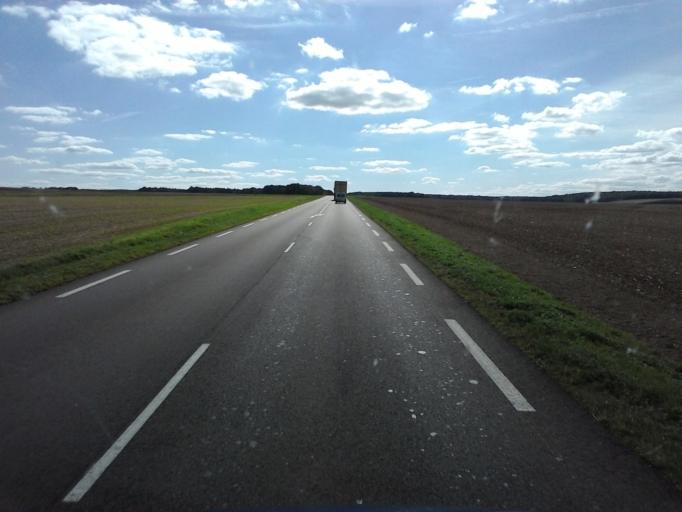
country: FR
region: Bourgogne
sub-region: Departement de la Cote-d'Or
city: Chatillon-sur-Seine
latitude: 47.8055
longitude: 4.5261
